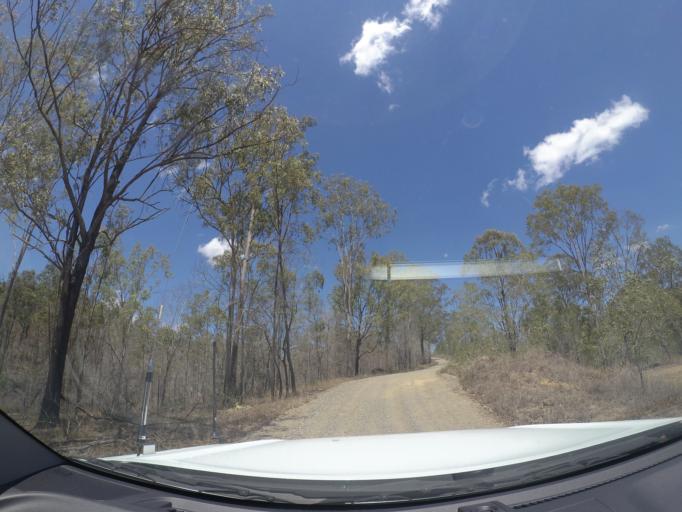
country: AU
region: Queensland
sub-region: Ipswich
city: Springfield Lakes
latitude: -27.8199
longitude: 152.8457
